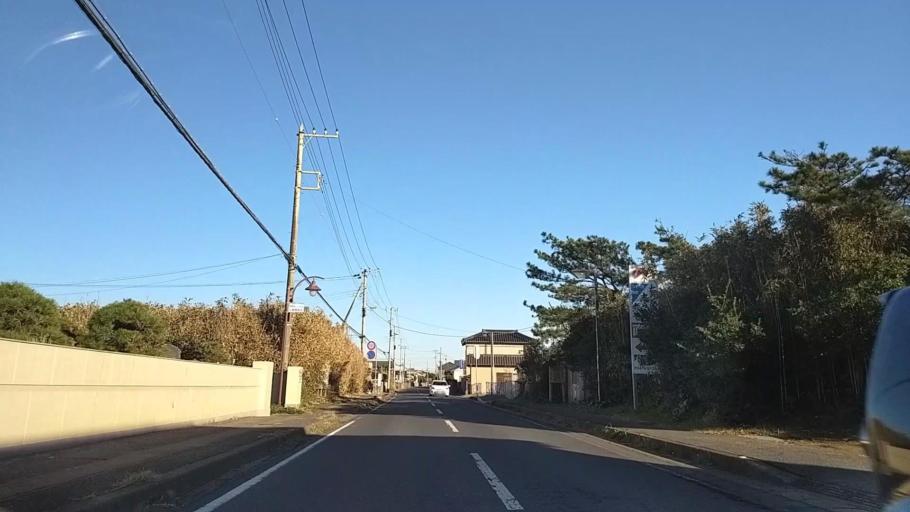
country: JP
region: Chiba
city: Asahi
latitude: 35.7019
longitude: 140.6996
